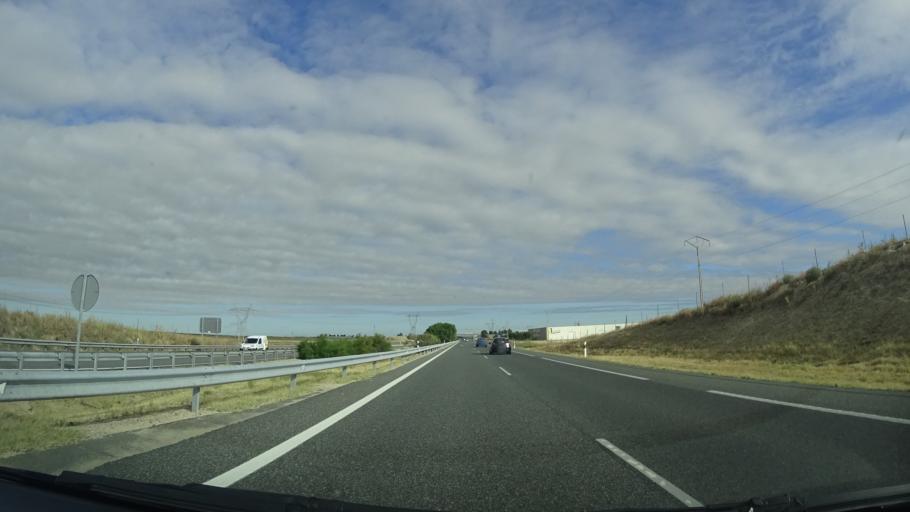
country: ES
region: Castille and Leon
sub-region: Provincia de Valladolid
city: San Vicente del Palacio
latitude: 41.2321
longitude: -4.8541
